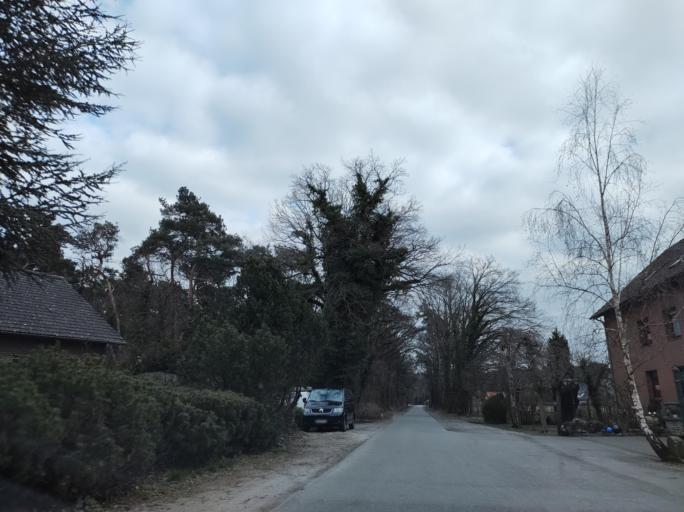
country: DE
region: North Rhine-Westphalia
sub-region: Regierungsbezirk Detmold
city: Delbruck
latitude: 51.7413
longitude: 8.5689
